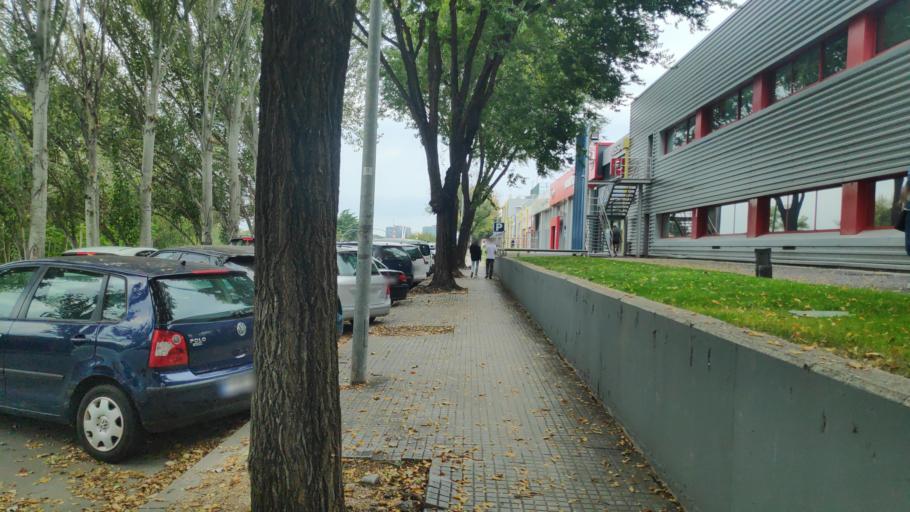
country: ES
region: Catalonia
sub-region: Provincia de Barcelona
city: Sant Cugat del Valles
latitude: 41.4799
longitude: 2.0608
